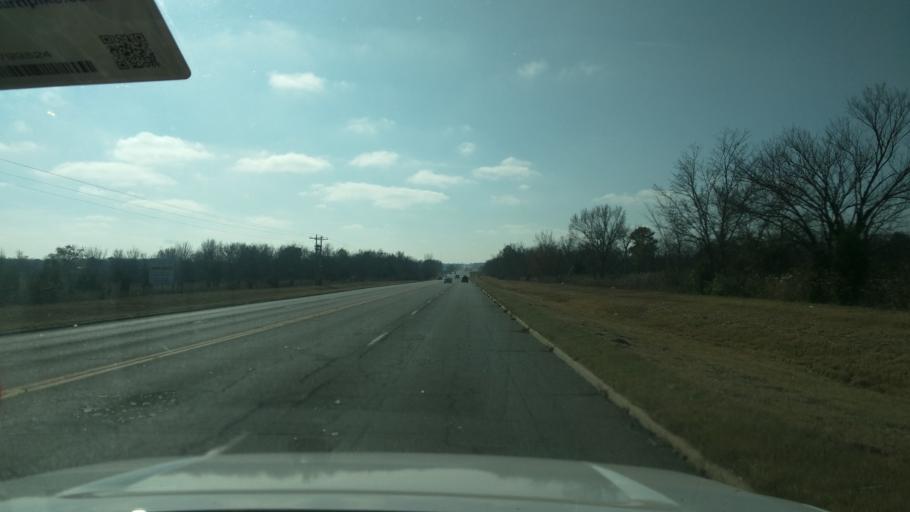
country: US
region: Oklahoma
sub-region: Washington County
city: Bartlesville
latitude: 36.6763
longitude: -95.9353
